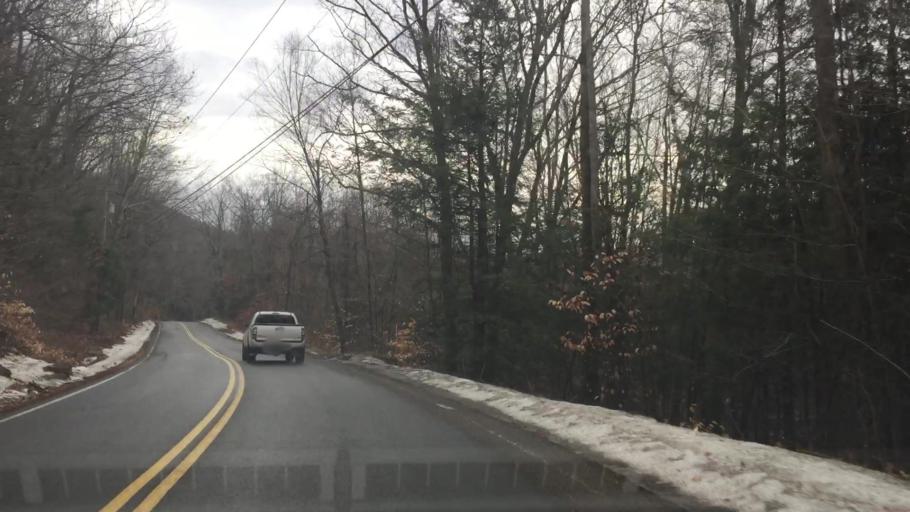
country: US
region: Massachusetts
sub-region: Hampshire County
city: Southampton
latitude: 42.2042
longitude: -72.8462
